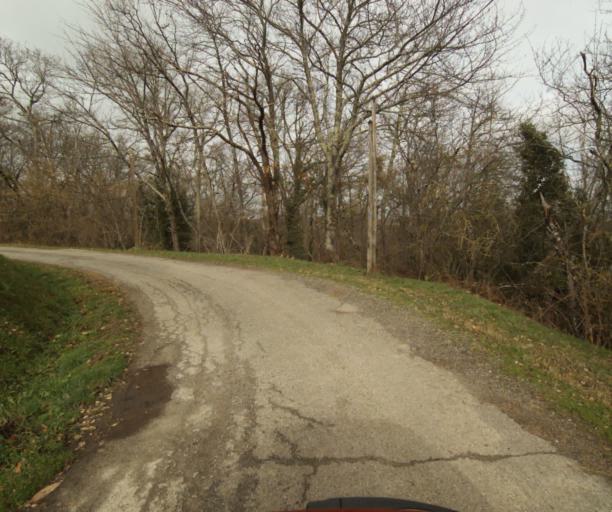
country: FR
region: Midi-Pyrenees
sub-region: Departement de l'Ariege
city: Pamiers
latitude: 43.0998
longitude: 1.5425
